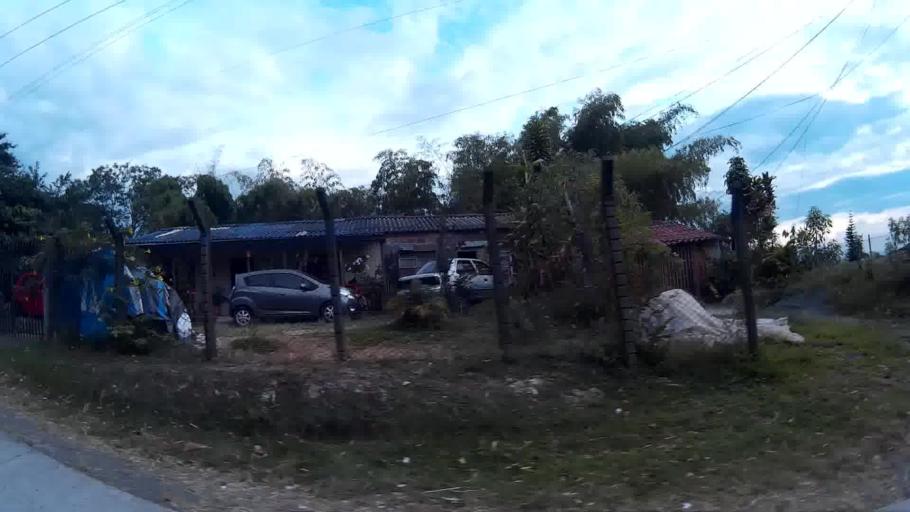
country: CO
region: Risaralda
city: Pereira
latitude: 4.7595
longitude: -75.6827
